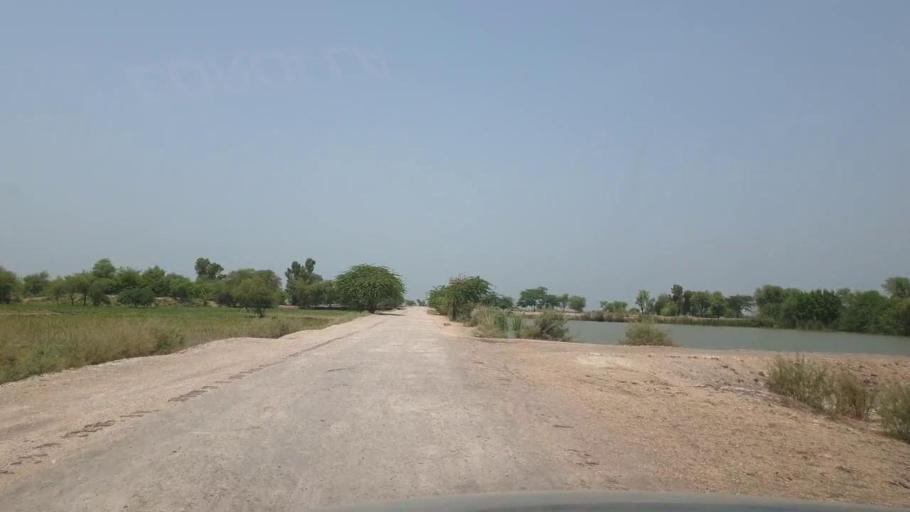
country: PK
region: Sindh
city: Garhi Yasin
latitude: 27.8769
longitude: 68.4456
